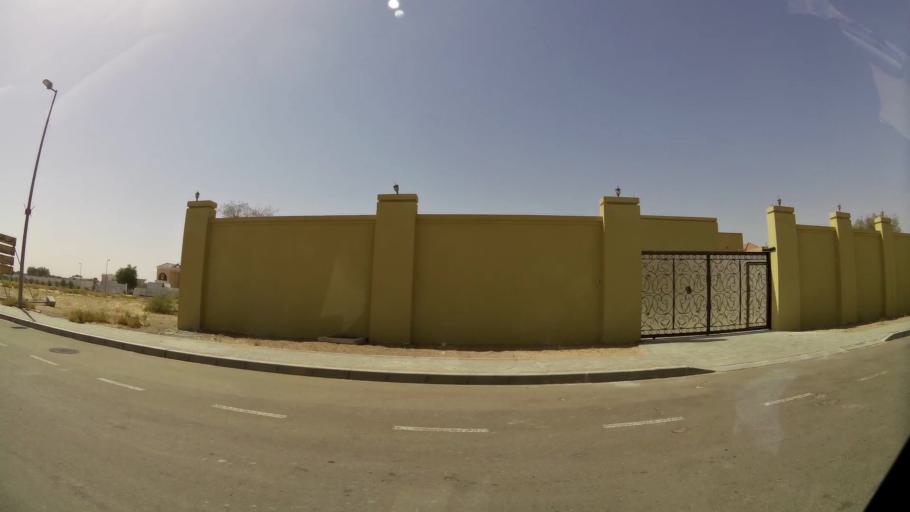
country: OM
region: Al Buraimi
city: Al Buraymi
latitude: 24.3037
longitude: 55.7527
